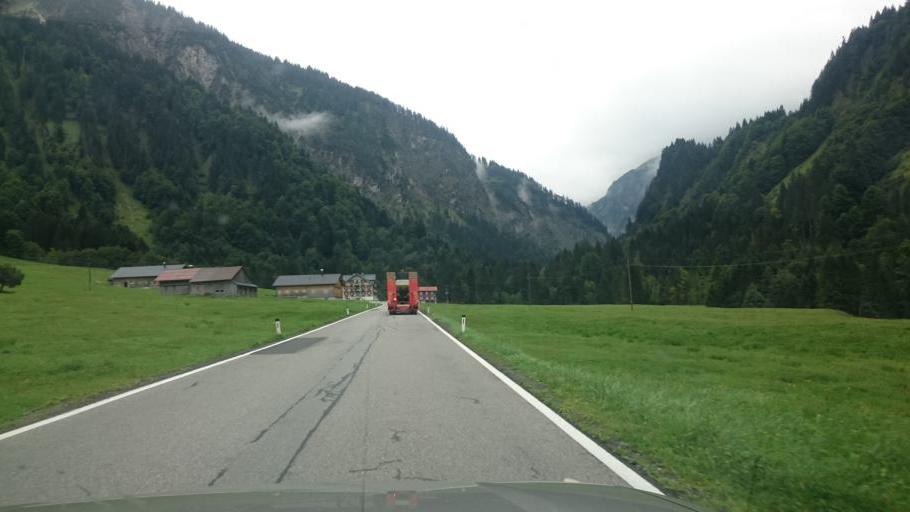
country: AT
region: Vorarlberg
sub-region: Politischer Bezirk Bregenz
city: Schroecken
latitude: 47.2834
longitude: 10.0553
